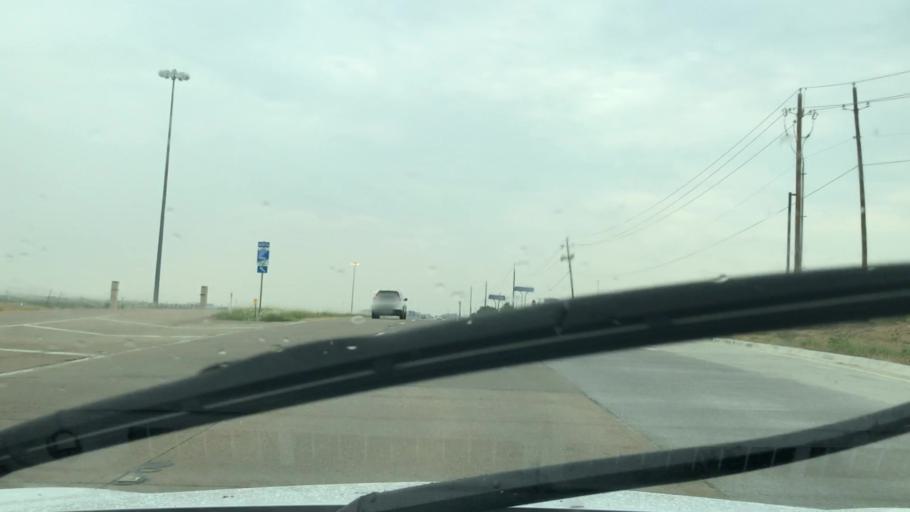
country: US
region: Texas
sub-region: Dallas County
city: Irving
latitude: 32.8727
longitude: -96.9948
